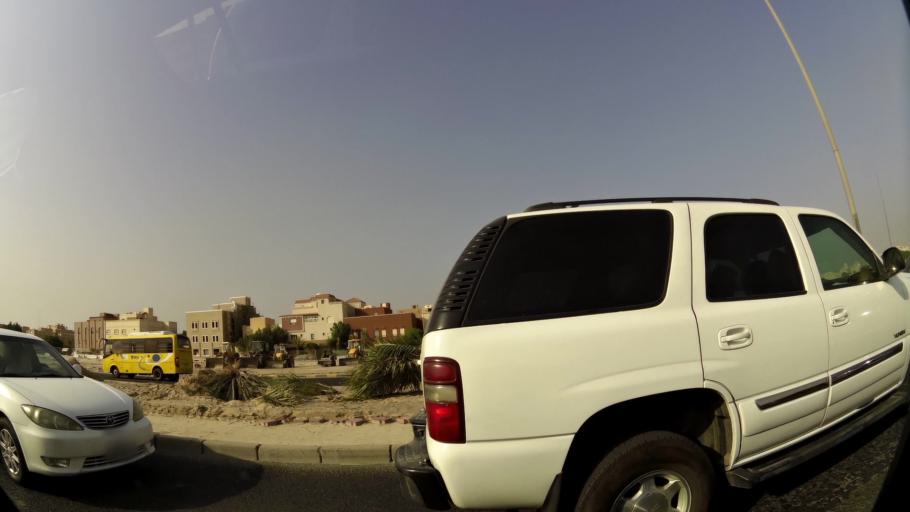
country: KW
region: Al Asimah
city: Ar Rabiyah
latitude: 29.2953
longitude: 47.8632
